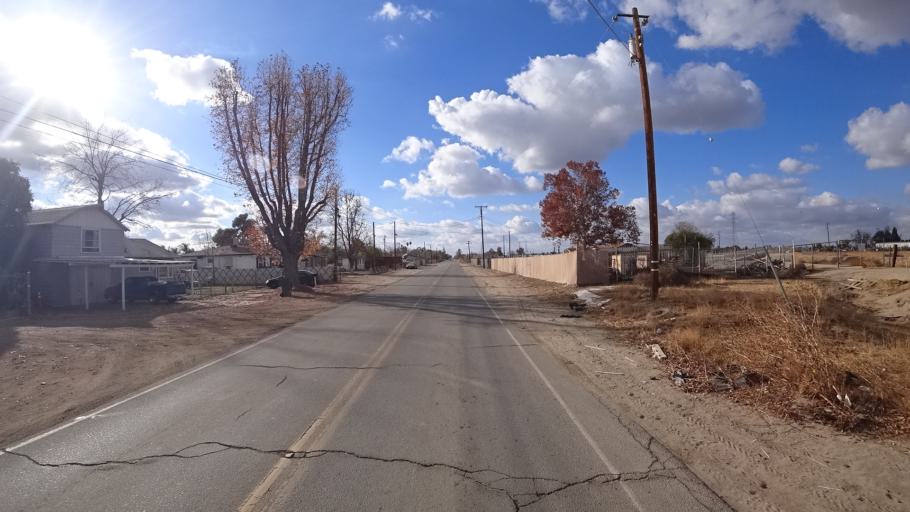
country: US
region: California
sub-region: Kern County
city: Greenfield
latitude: 35.3104
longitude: -118.9925
